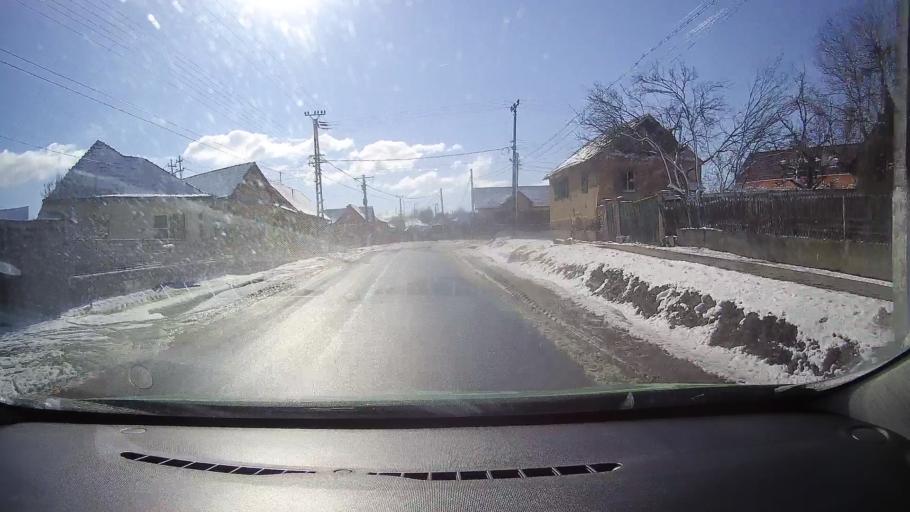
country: RO
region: Sibiu
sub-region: Comuna Rosia
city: Rosia
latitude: 45.8024
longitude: 24.2874
